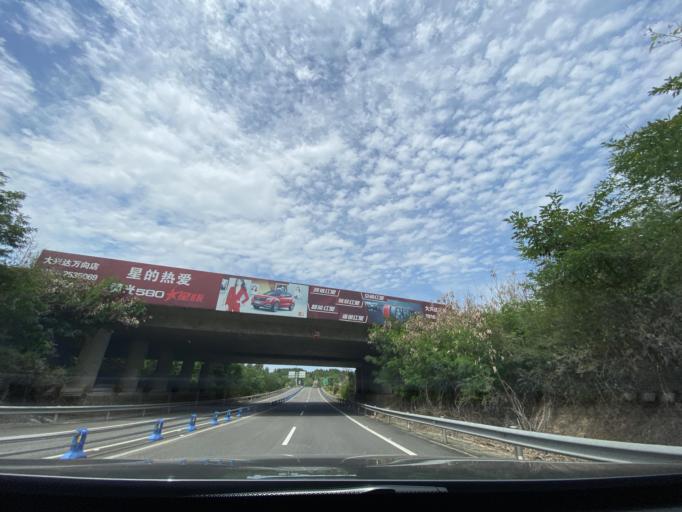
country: CN
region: Sichuan
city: Mianyang
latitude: 31.3500
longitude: 104.7082
